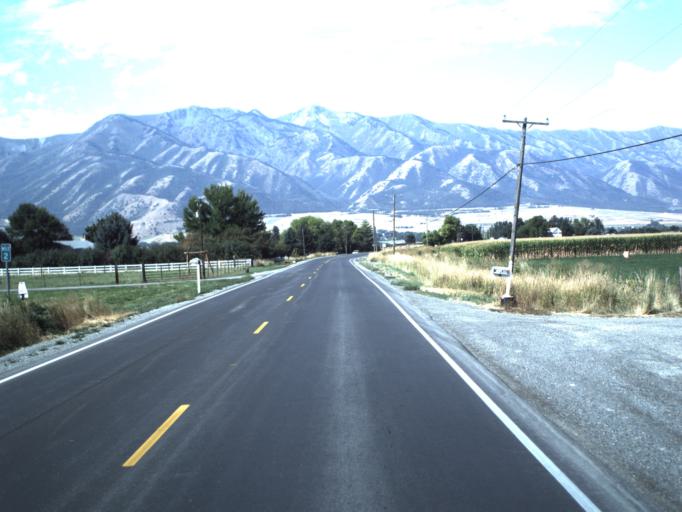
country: US
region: Utah
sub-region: Cache County
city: Wellsville
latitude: 41.6413
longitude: -111.8995
